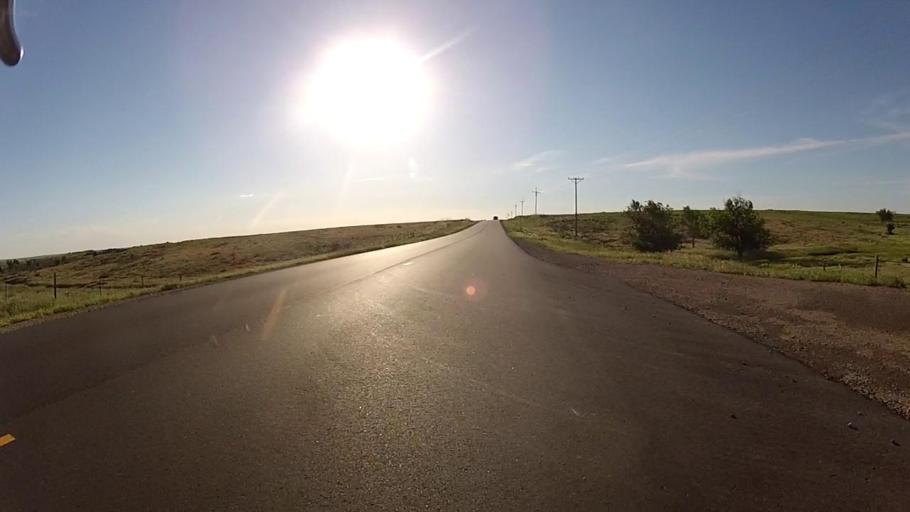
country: US
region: Kansas
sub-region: Comanche County
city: Coldwater
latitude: 37.2823
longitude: -99.1291
